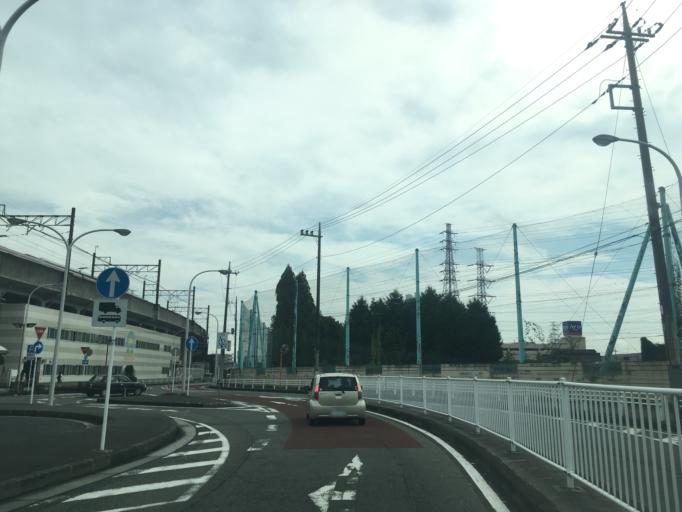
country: JP
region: Tokyo
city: Hachioji
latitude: 35.5939
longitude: 139.3451
